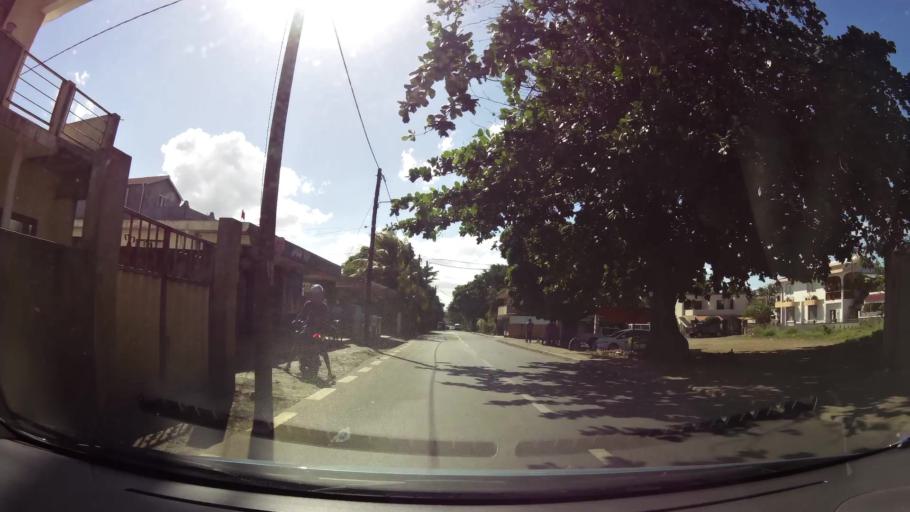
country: MU
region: Black River
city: Cascavelle
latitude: -20.2619
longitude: 57.4170
